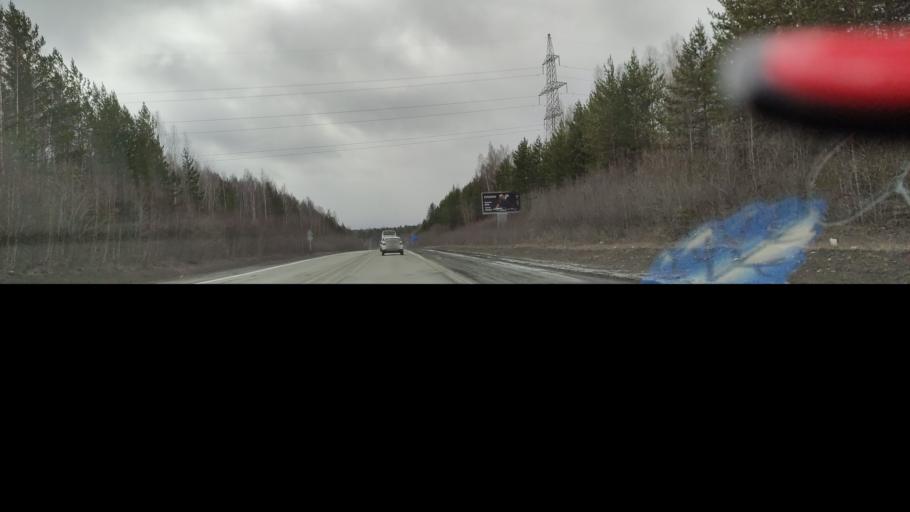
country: RU
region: Sverdlovsk
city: Talitsa
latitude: 56.8517
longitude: 60.0587
